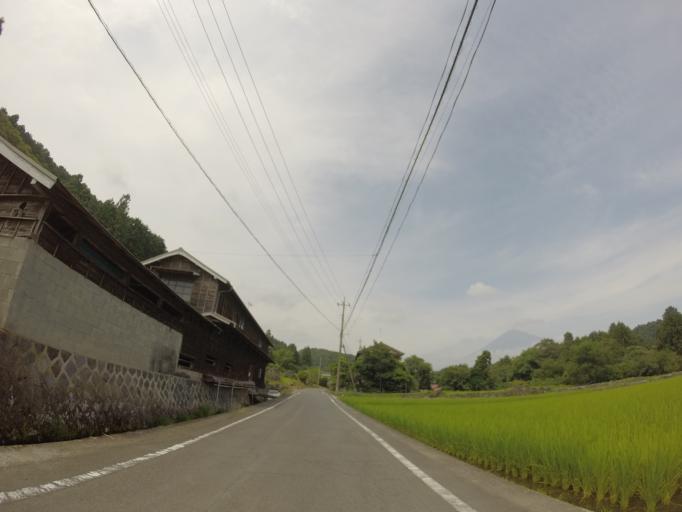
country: JP
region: Shizuoka
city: Fujinomiya
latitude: 35.2765
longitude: 138.5637
